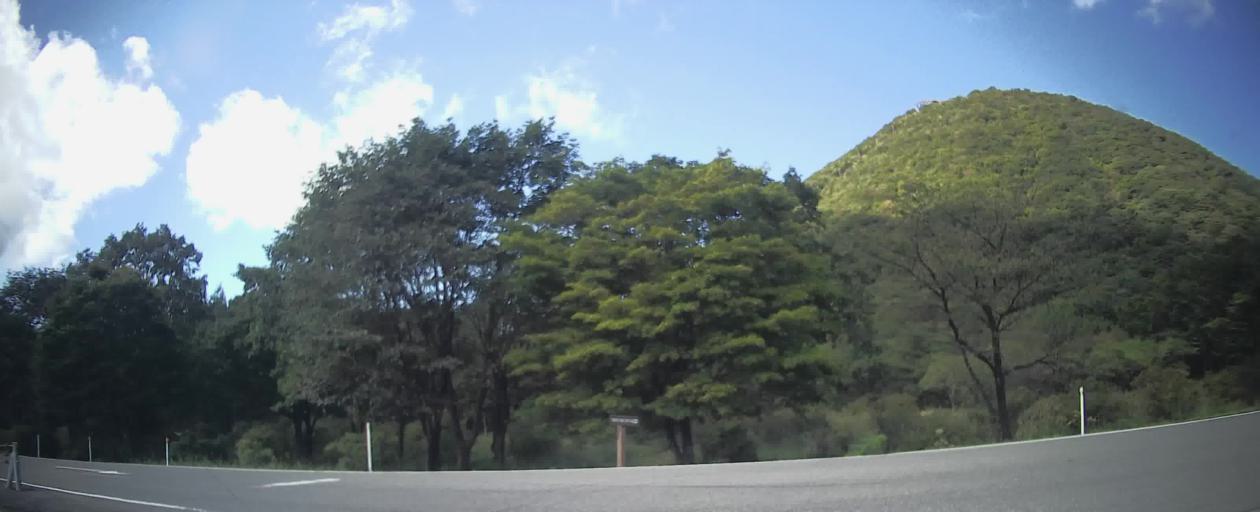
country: JP
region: Gunma
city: Shibukawa
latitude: 36.4700
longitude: 138.8818
